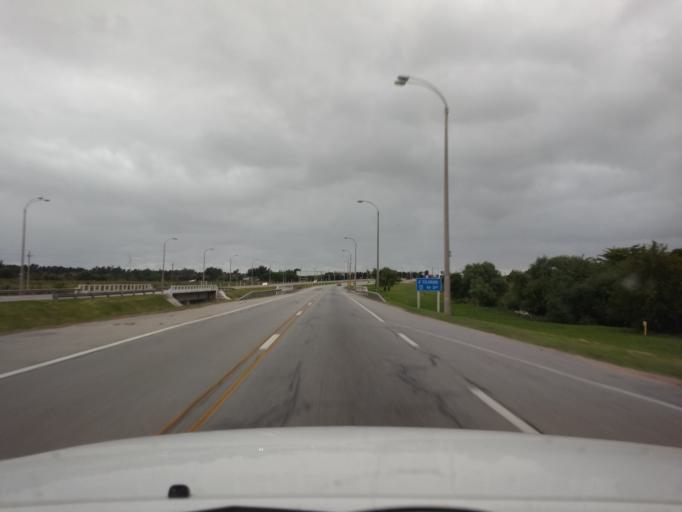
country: UY
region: Canelones
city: Progreso
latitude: -34.6916
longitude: -56.2390
